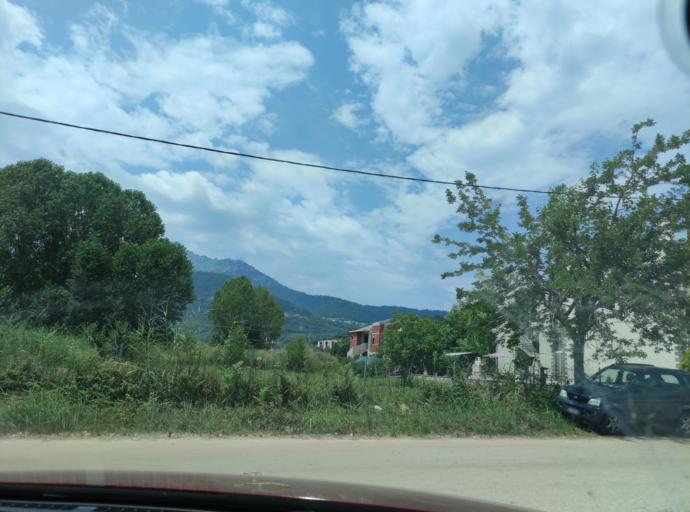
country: GR
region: East Macedonia and Thrace
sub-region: Nomos Kavalas
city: Potamia
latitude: 40.7237
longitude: 24.7564
